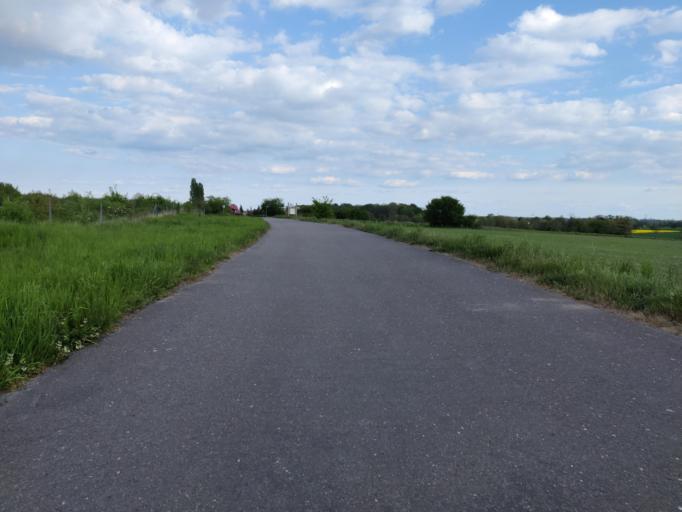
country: DE
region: Saxony
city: Espenhain
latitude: 51.2233
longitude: 12.4585
